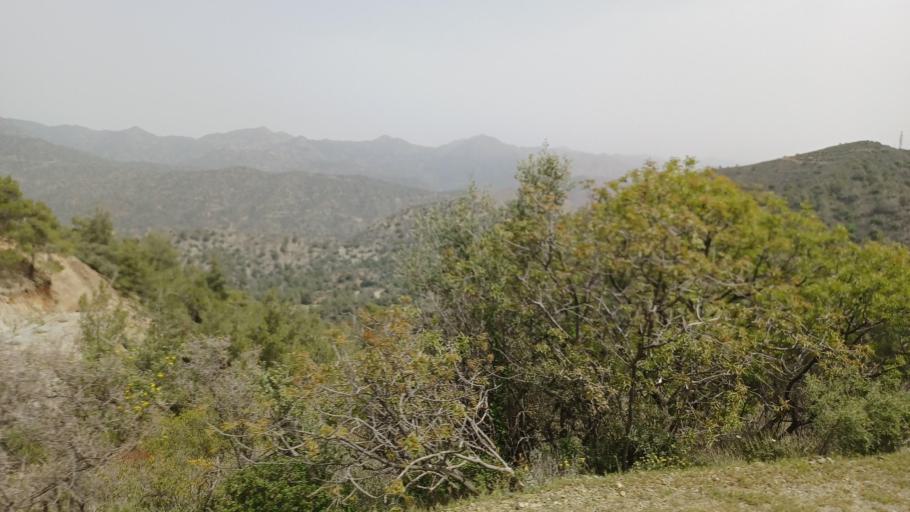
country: CY
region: Limassol
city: Parekklisha
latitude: 34.8289
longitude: 33.0951
